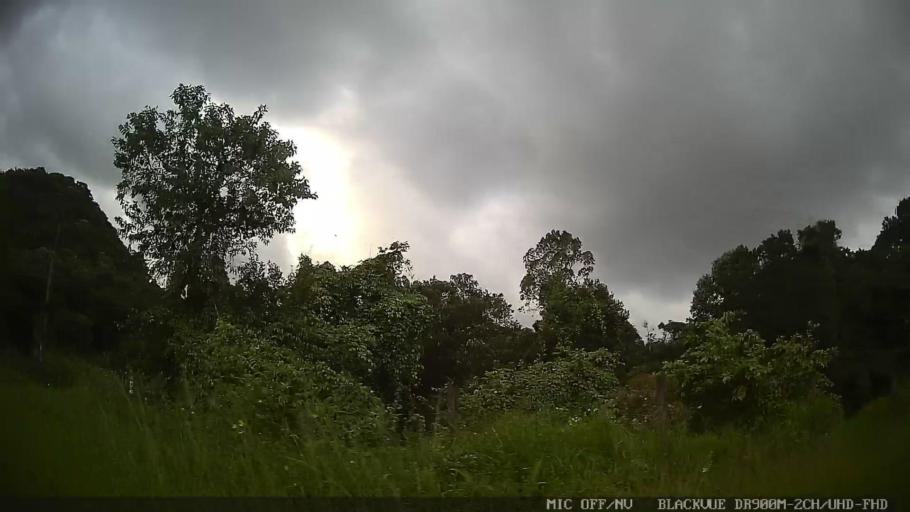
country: BR
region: Sao Paulo
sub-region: Itanhaem
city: Itanhaem
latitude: -24.1438
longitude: -46.7765
